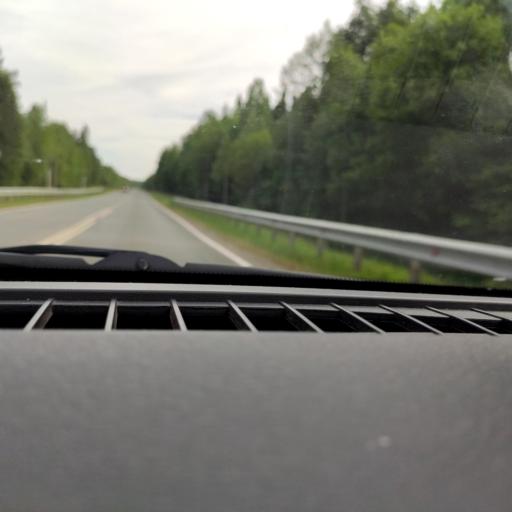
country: RU
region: Perm
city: Polazna
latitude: 58.3069
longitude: 56.1543
